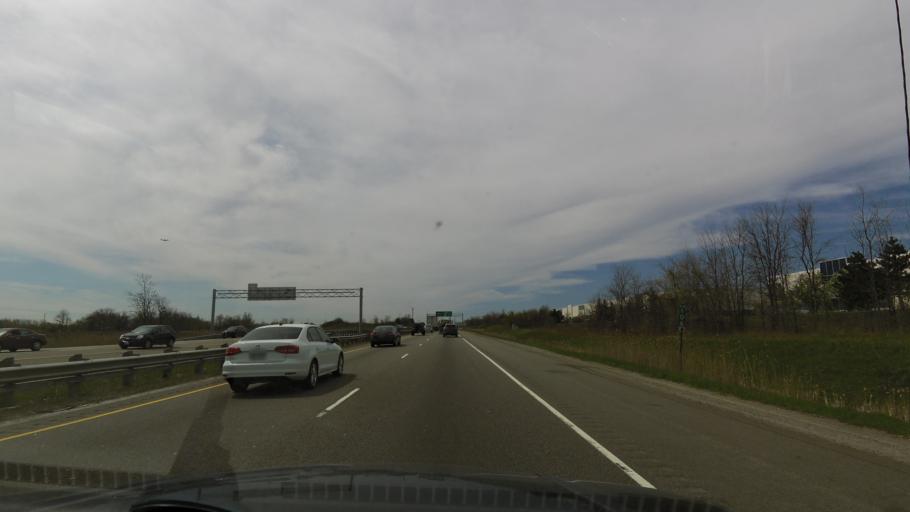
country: CA
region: Ontario
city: Oakville
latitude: 43.5168
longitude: -79.7022
